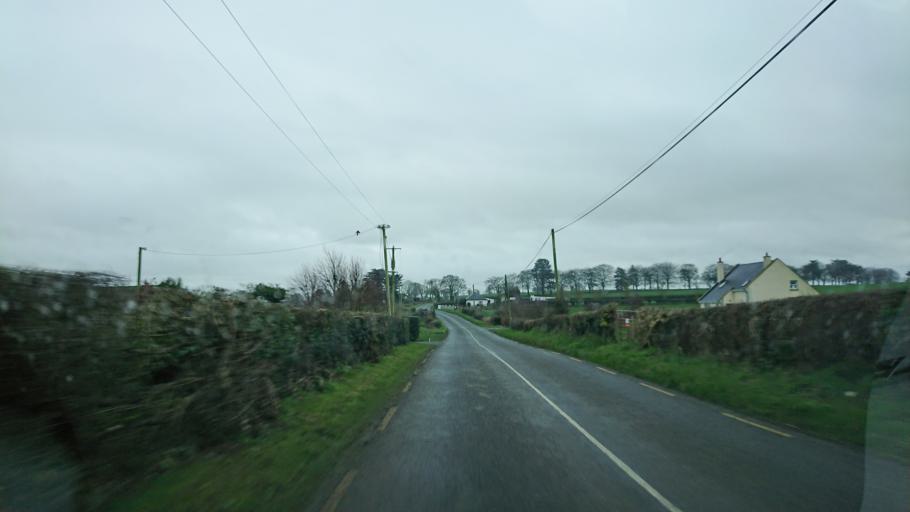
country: IE
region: Leinster
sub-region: Kilkenny
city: Callan
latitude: 52.5281
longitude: -7.2989
